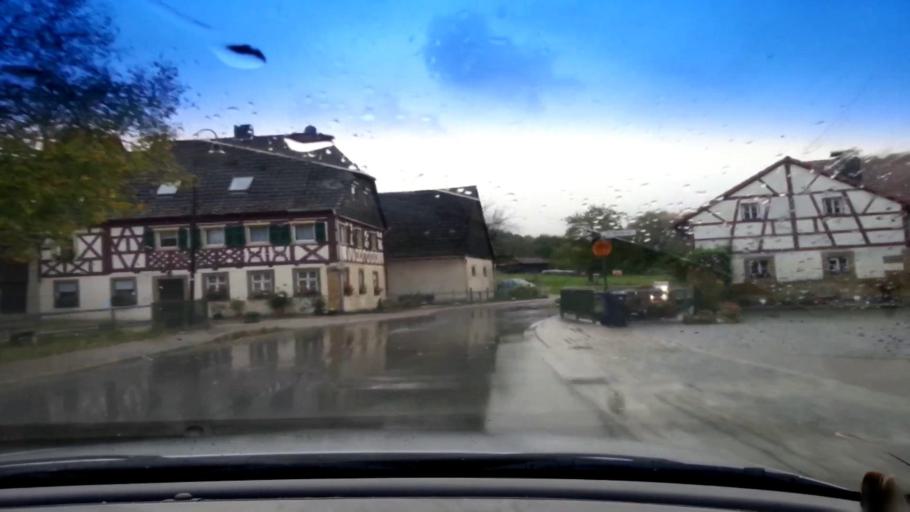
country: DE
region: Bavaria
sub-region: Upper Franconia
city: Schesslitz
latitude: 50.0074
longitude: 11.0696
